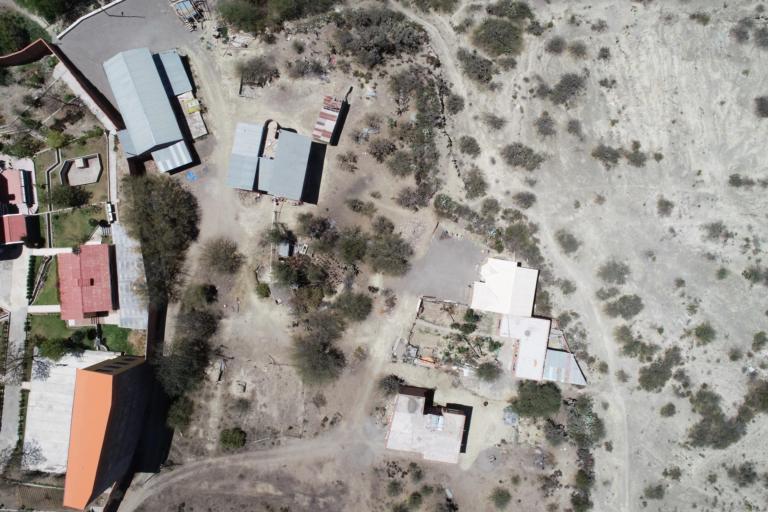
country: BO
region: La Paz
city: La Paz
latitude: -16.6471
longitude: -68.0420
